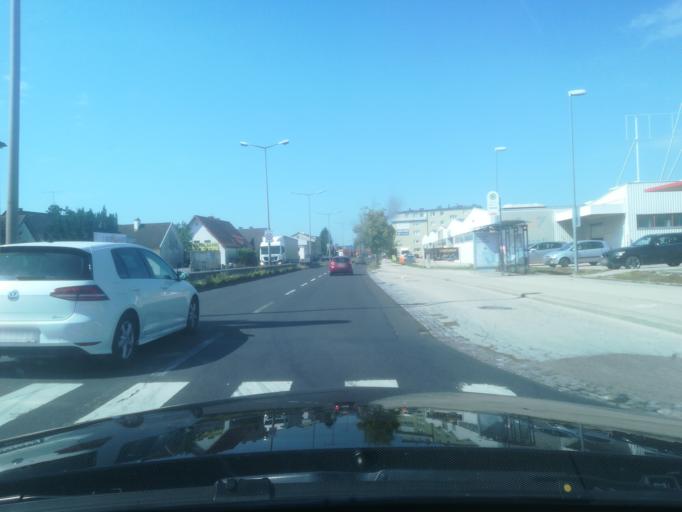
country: AT
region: Upper Austria
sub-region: Wels Stadt
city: Wels
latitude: 48.1752
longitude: 14.0560
